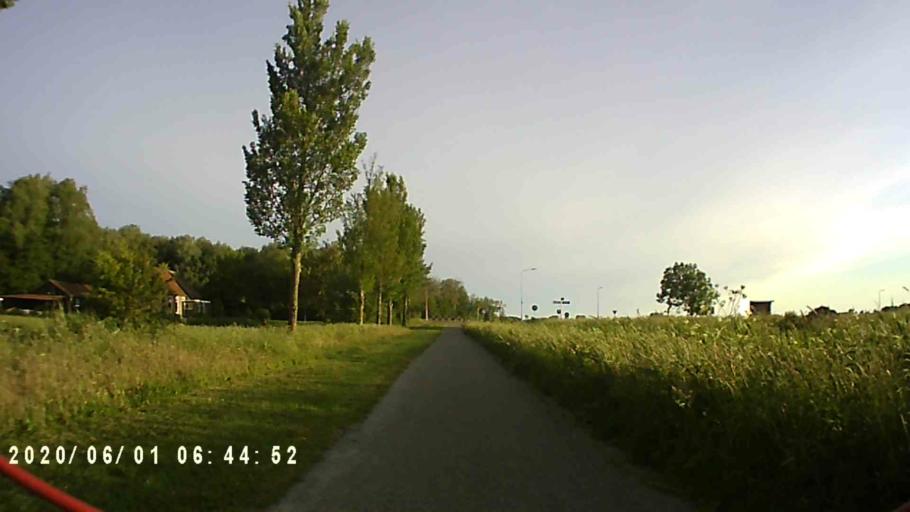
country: NL
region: Friesland
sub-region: Gemeente Kollumerland en Nieuwkruisland
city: Kollum
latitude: 53.3024
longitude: 6.1475
